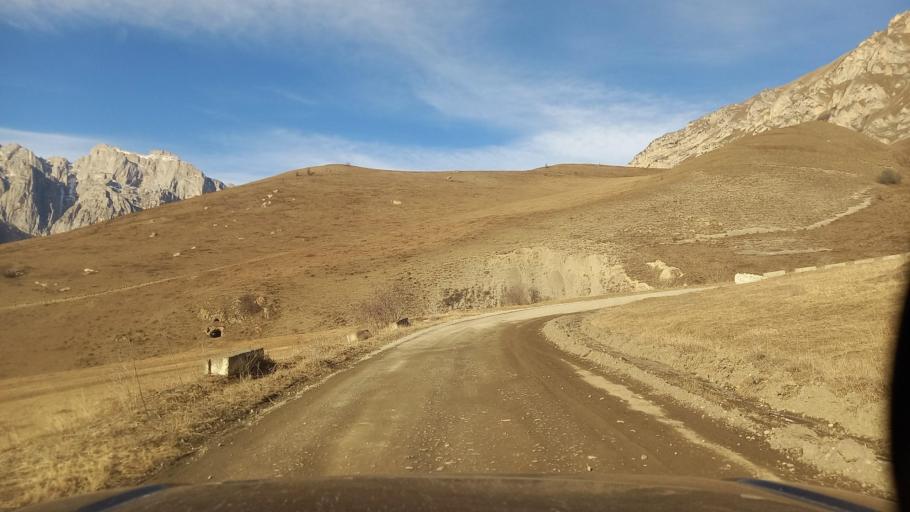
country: RU
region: North Ossetia
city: Verkhniy Fiagdon
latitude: 42.8390
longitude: 44.4640
